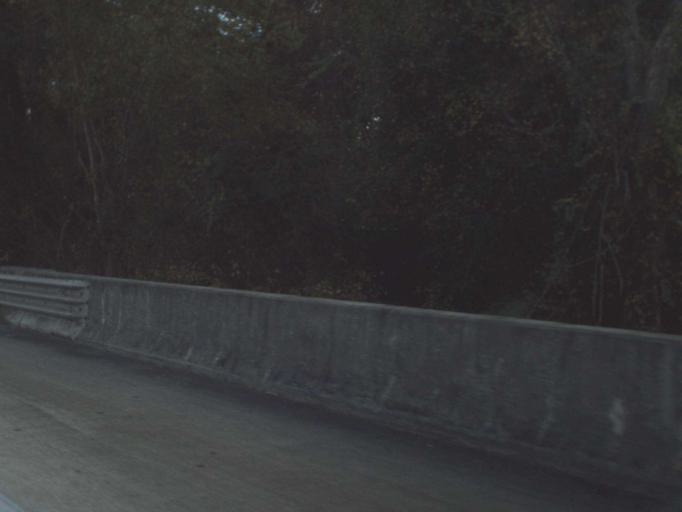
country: US
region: Florida
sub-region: Jefferson County
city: Monticello
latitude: 30.4837
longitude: -83.9483
